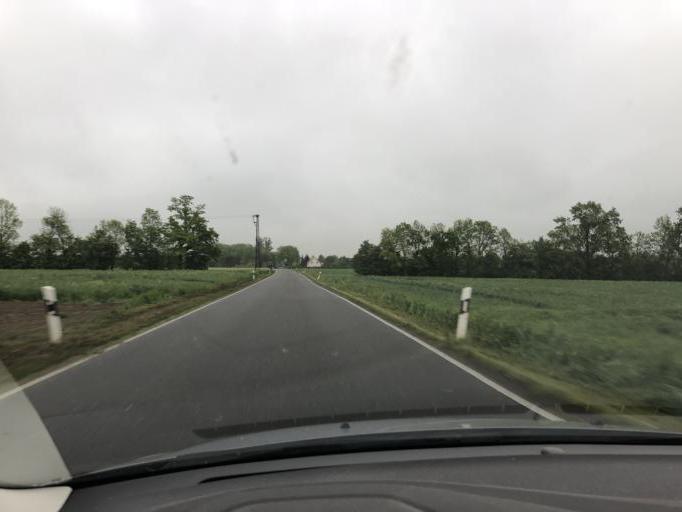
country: DE
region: Saxony
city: Jesewitz
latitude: 51.4338
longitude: 12.5404
